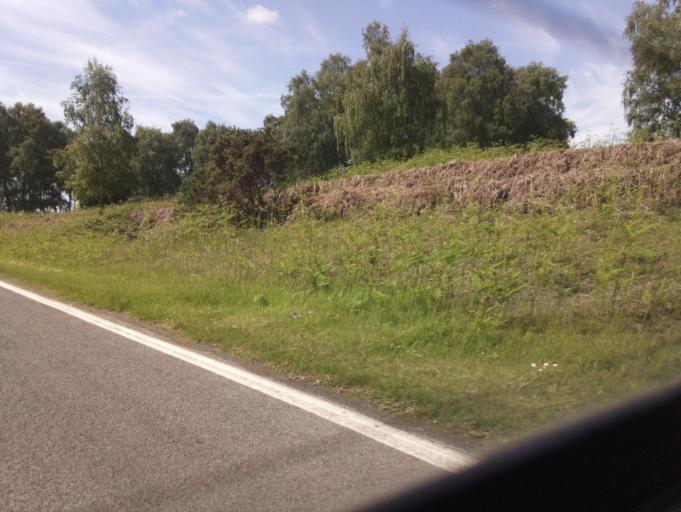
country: GB
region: England
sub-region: North Lincolnshire
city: Manton
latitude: 53.5260
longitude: -0.5789
